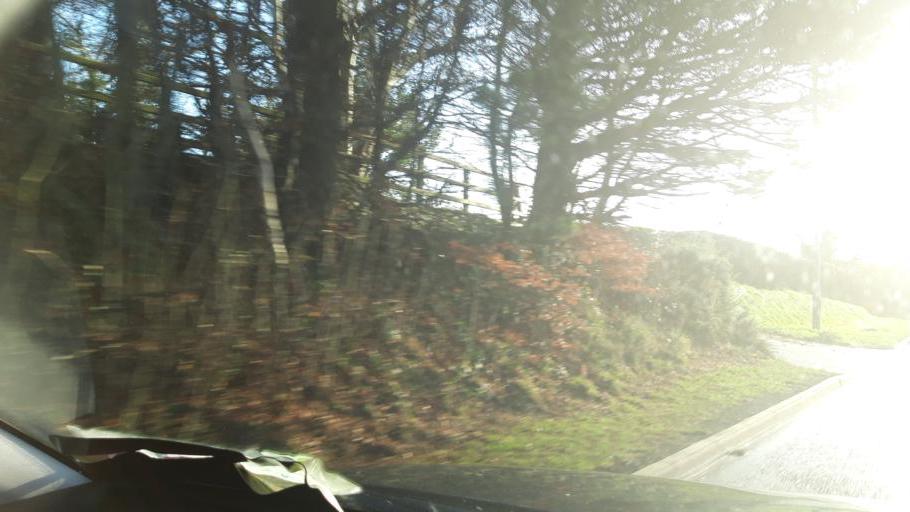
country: GB
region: Northern Ireland
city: Maghera
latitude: 54.9042
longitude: -6.6682
